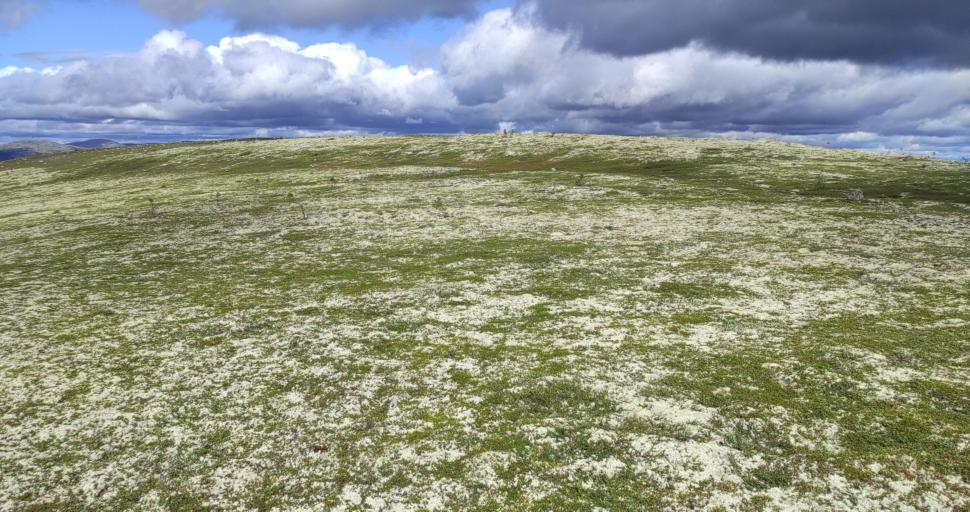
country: RU
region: Murmansk
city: Afrikanda
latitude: 67.0508
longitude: 32.9615
